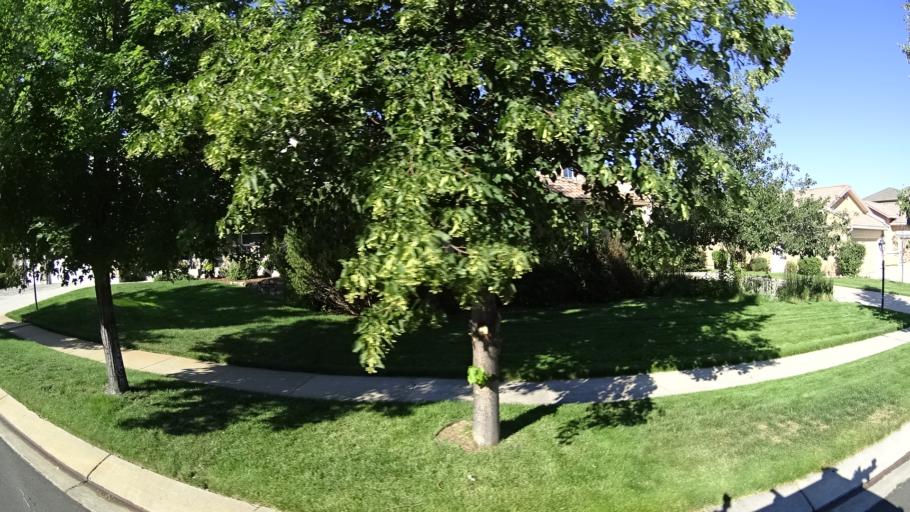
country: US
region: Colorado
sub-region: El Paso County
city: Black Forest
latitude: 38.9798
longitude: -104.7669
